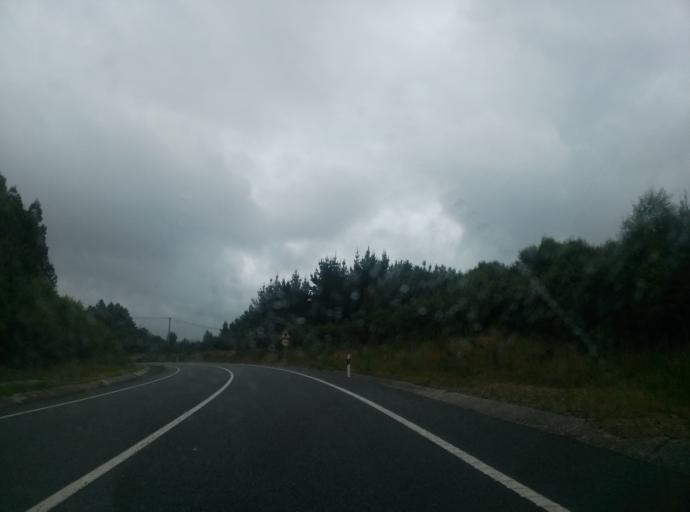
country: ES
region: Galicia
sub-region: Provincia de Lugo
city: Viveiro
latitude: 43.5983
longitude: -7.6095
